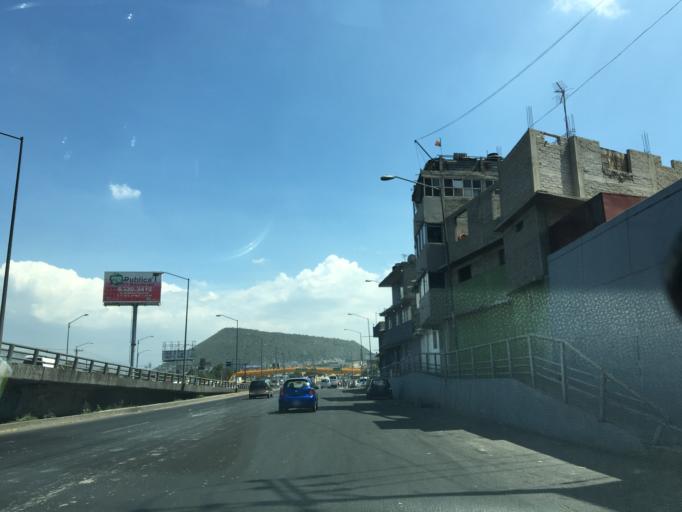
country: MX
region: Mexico
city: Los Reyes La Paz
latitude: 19.3572
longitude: -98.9939
